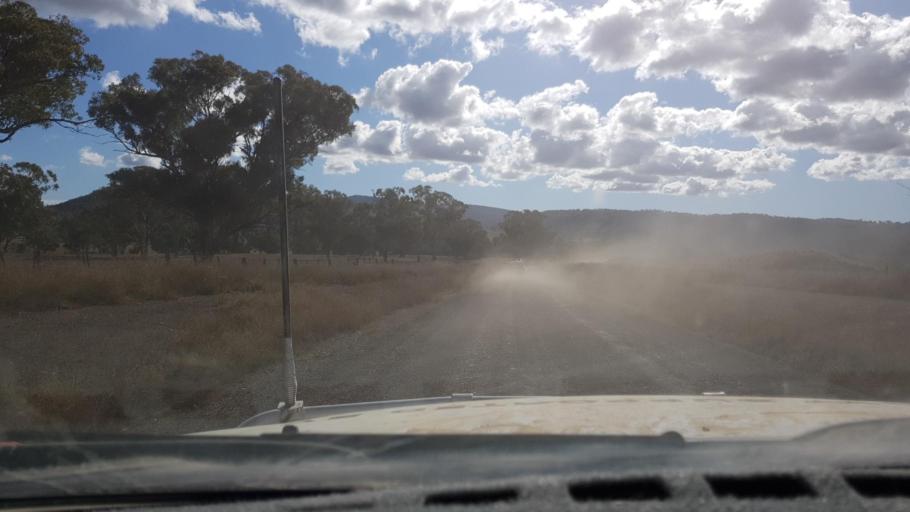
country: AU
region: New South Wales
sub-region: Tamworth Municipality
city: Manilla
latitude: -30.6263
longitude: 150.5105
